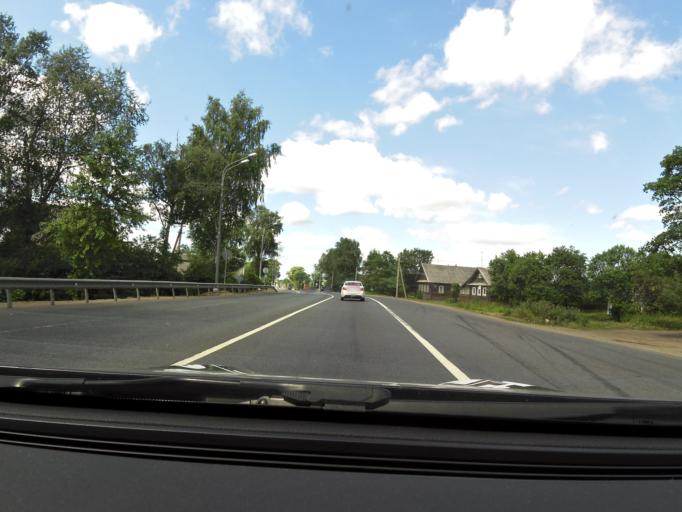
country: RU
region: Tverskaya
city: Kuzhenkino
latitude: 57.7235
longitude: 34.0822
